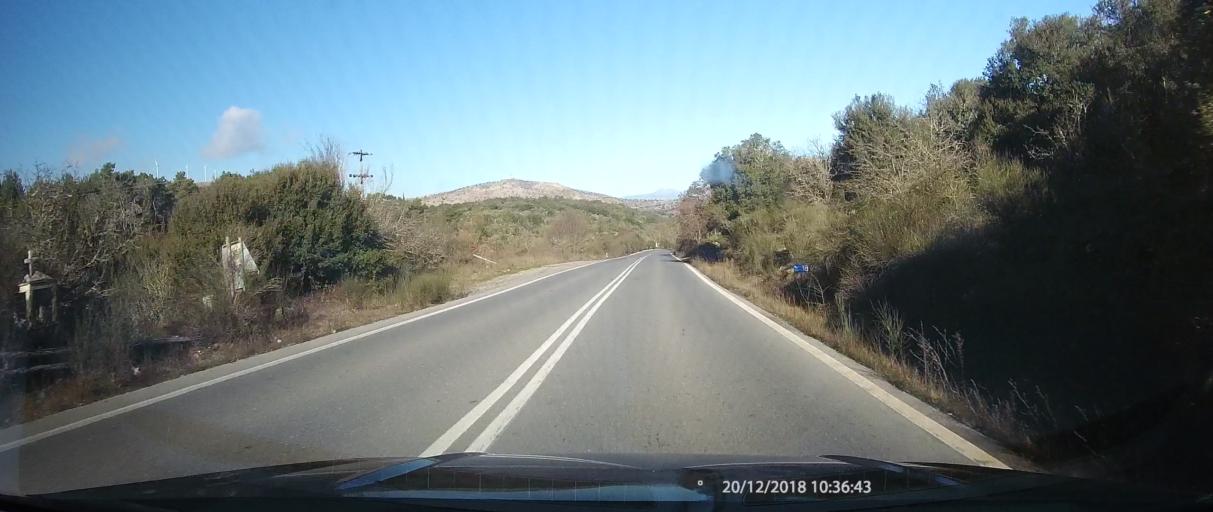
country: GR
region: Peloponnese
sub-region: Nomos Lakonias
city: Kariai
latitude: 37.3697
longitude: 22.3986
